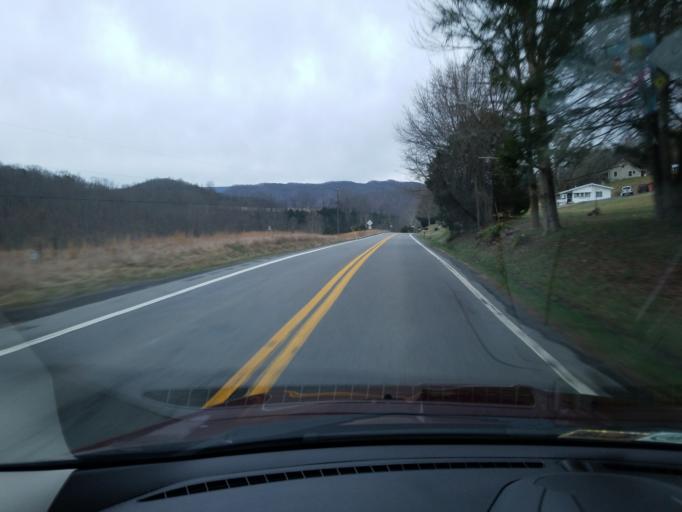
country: US
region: West Virginia
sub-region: Monroe County
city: Union
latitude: 37.5665
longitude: -80.5687
